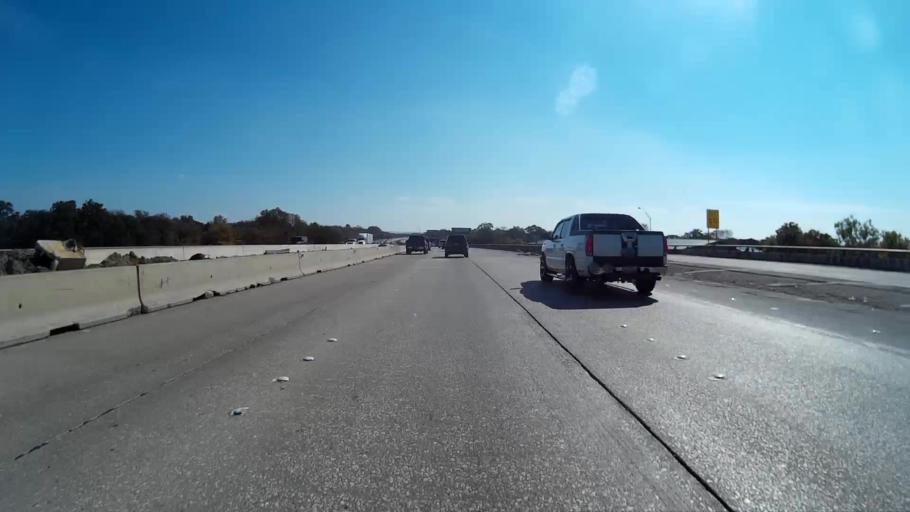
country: US
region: Texas
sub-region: Dallas County
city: Dallas
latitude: 32.7613
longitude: -96.7748
